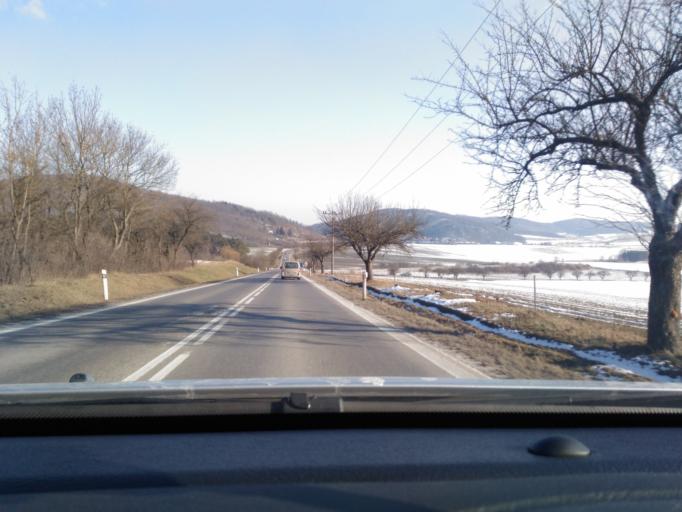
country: CZ
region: South Moravian
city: Cebin
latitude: 49.3084
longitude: 16.5000
